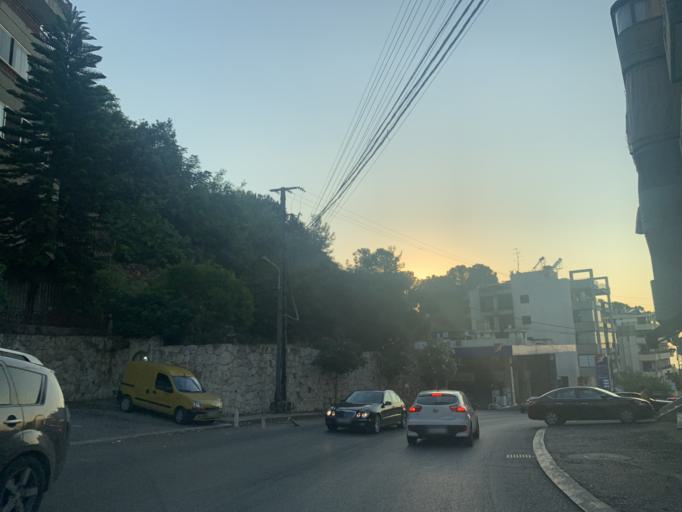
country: LB
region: Mont-Liban
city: Djounie
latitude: 33.9561
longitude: 35.6410
